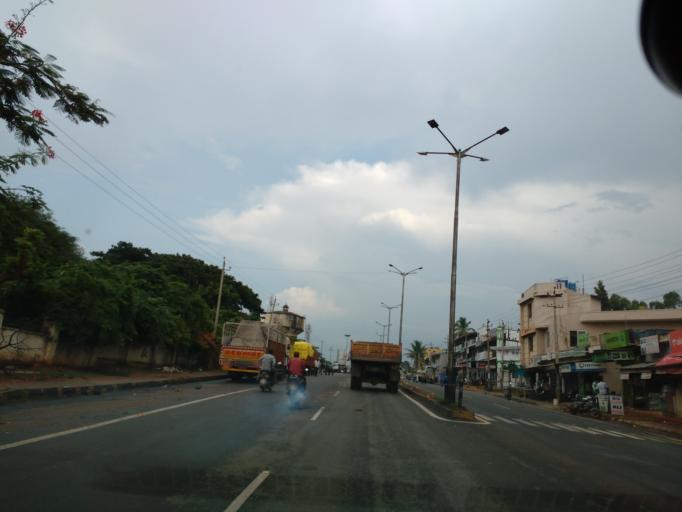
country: IN
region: Karnataka
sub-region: Hassan
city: Arsikere
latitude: 13.3196
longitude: 76.2522
